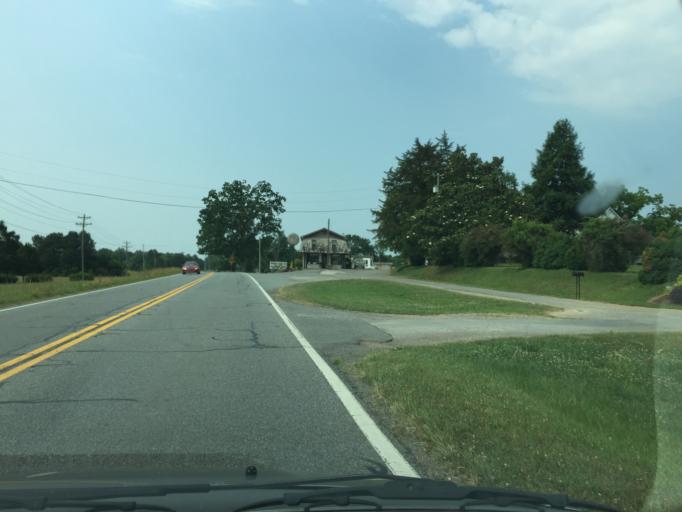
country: US
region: Georgia
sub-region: Catoosa County
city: Ringgold
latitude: 34.8734
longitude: -85.1415
